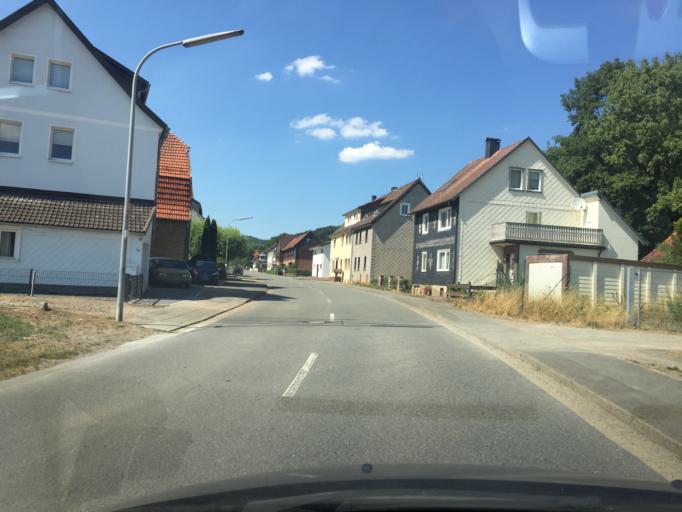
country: DE
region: Lower Saxony
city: Bad Sachsa
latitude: 51.5873
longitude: 10.5225
